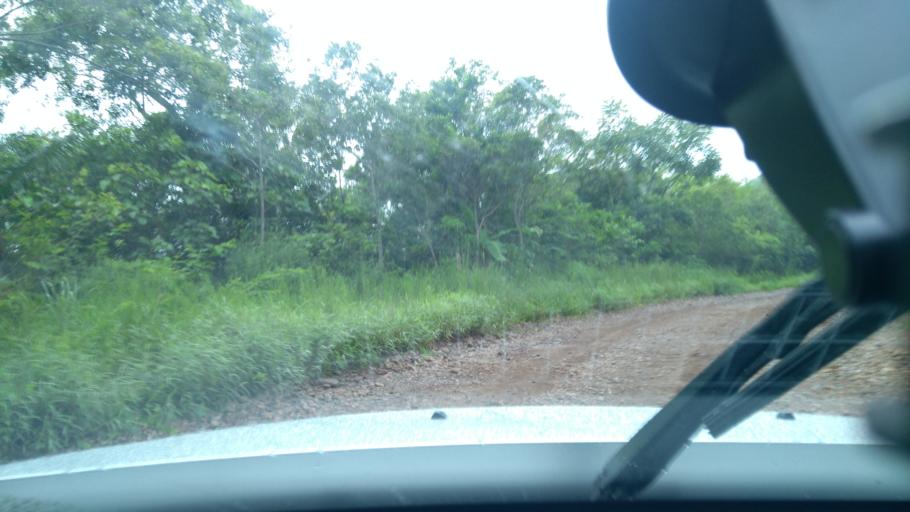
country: BR
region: Rio Grande do Sul
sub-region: Torres
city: Torres
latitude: -29.1939
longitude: -49.9749
